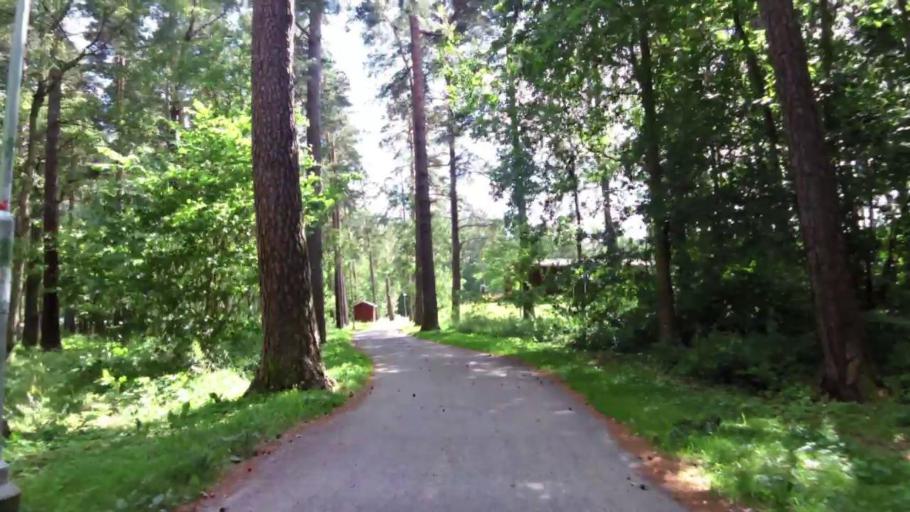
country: SE
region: OEstergoetland
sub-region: Linkopings Kommun
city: Linkoping
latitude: 58.4138
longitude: 15.5854
